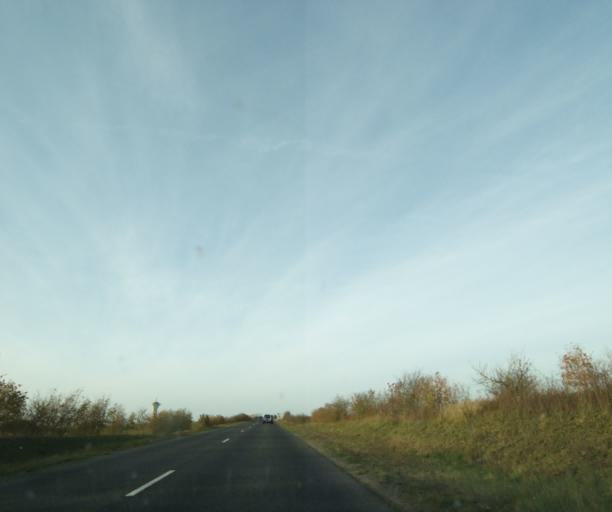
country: FR
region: Lorraine
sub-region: Departement de la Meuse
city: Etain
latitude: 49.2136
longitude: 5.6531
